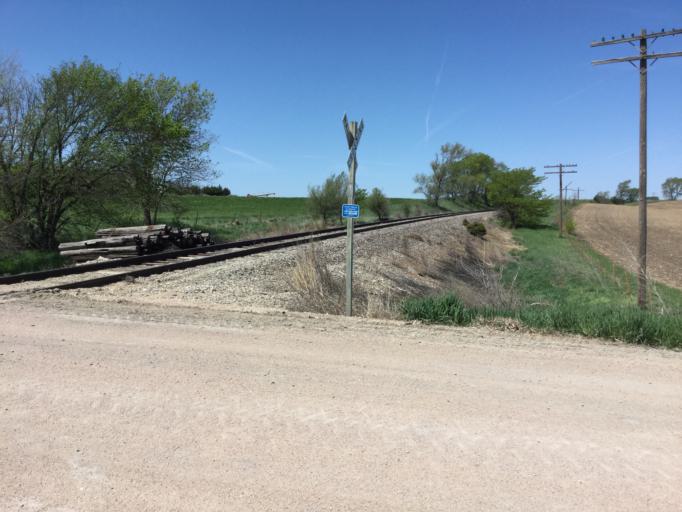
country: US
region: Kansas
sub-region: Smith County
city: Smith Center
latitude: 39.7496
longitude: -98.8607
